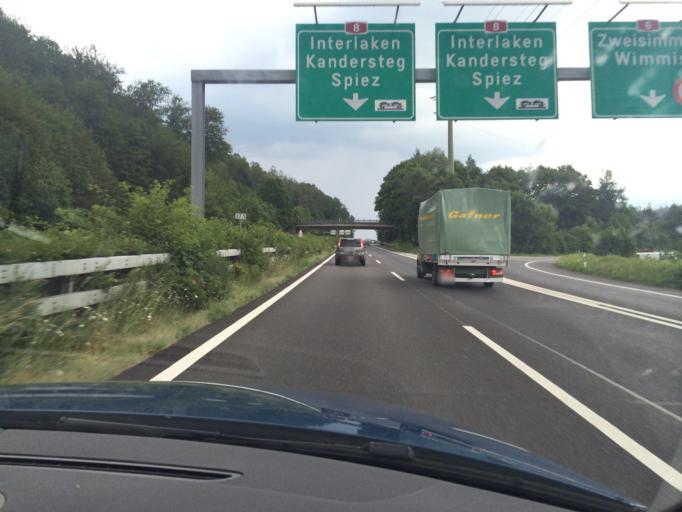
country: CH
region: Bern
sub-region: Frutigen-Niedersimmental District
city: Wimmis
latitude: 46.6944
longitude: 7.6481
